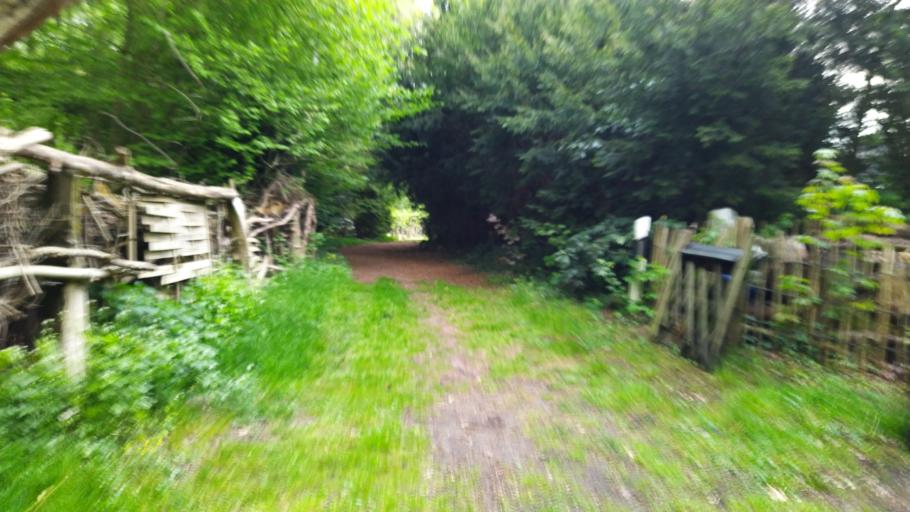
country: DE
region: Lower Saxony
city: Harsefeld
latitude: 53.4585
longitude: 9.4822
